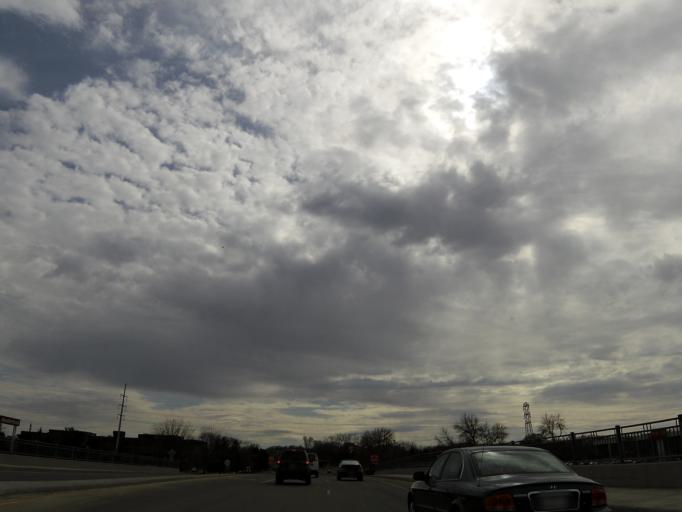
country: US
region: Minnesota
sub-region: Hennepin County
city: Bloomington
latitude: 44.8616
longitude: -93.3189
